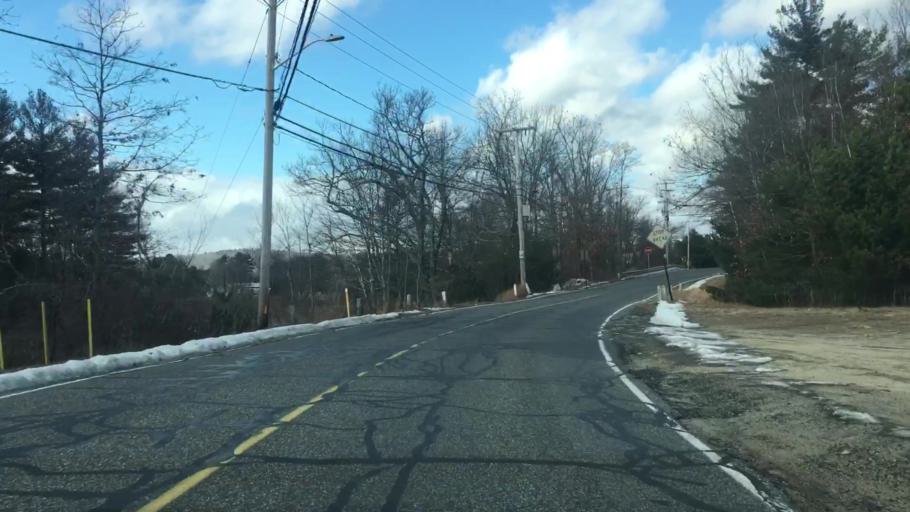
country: US
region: Massachusetts
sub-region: Hampden County
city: Brimfield
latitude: 42.1162
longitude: -72.1970
